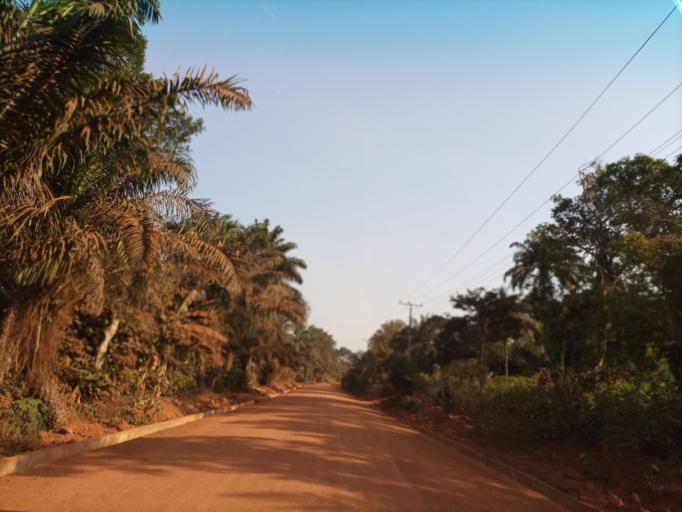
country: NG
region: Enugu
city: Opi
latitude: 6.7546
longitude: 7.4059
